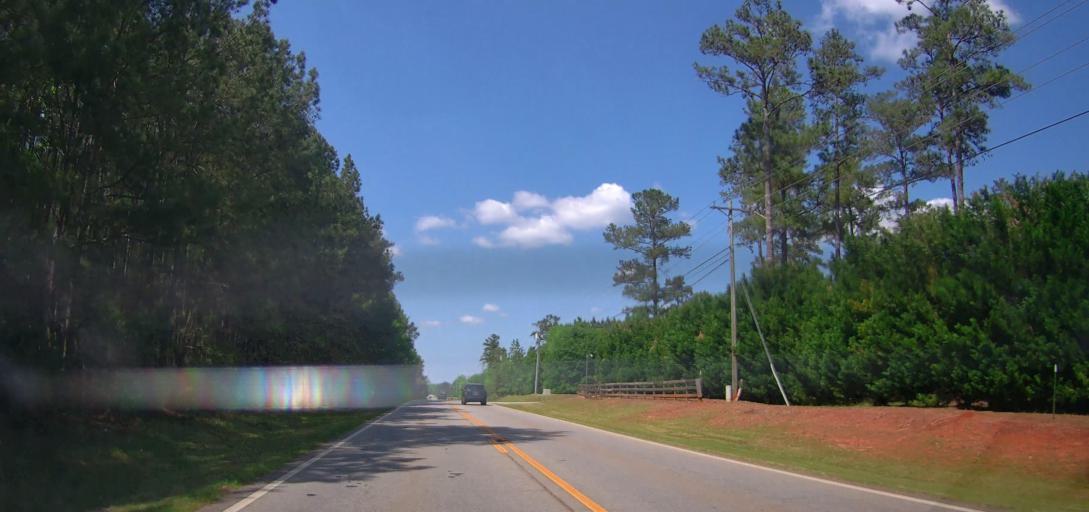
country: US
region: Georgia
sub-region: Putnam County
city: Eatonton
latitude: 33.2614
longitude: -83.3012
